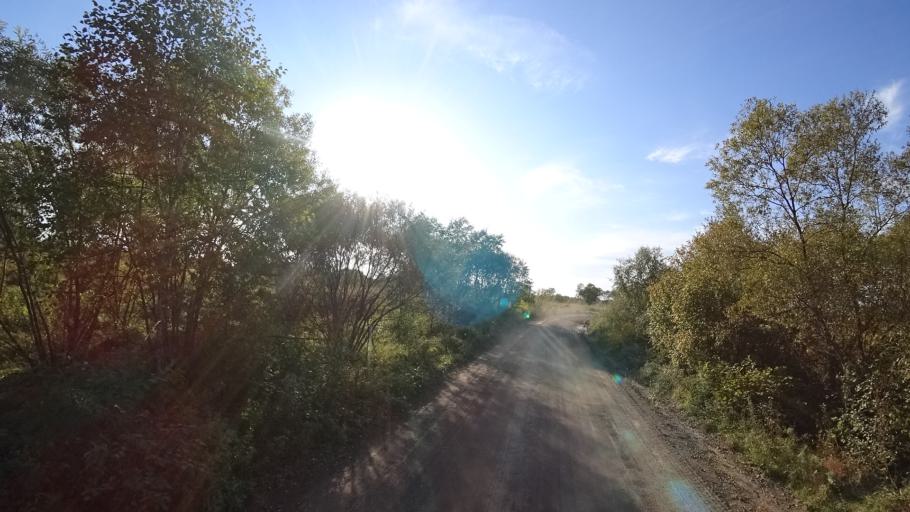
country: RU
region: Amur
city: Arkhara
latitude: 49.3542
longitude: 130.1351
